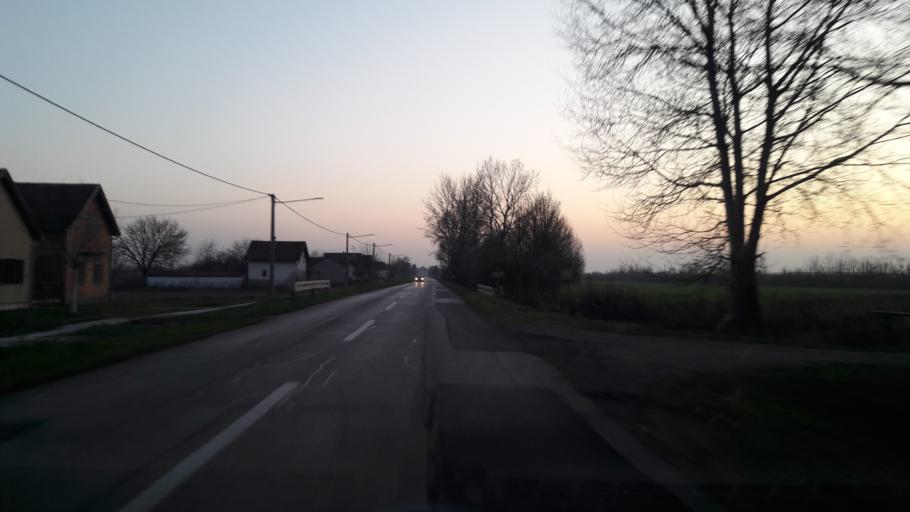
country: HR
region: Vukovarsko-Srijemska
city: Nijemci
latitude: 45.1904
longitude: 19.0175
